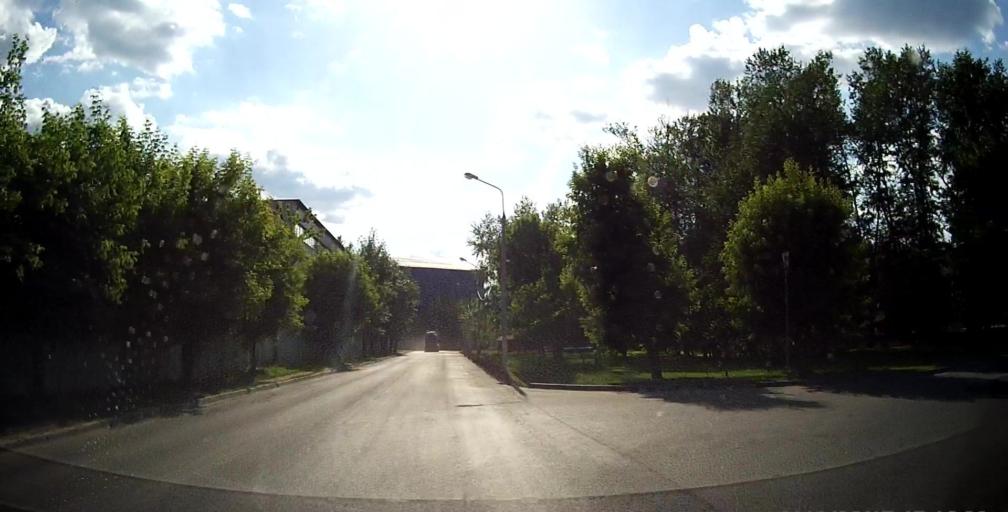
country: RU
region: Moskovskaya
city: Shcherbinka
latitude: 55.4998
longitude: 37.5658
